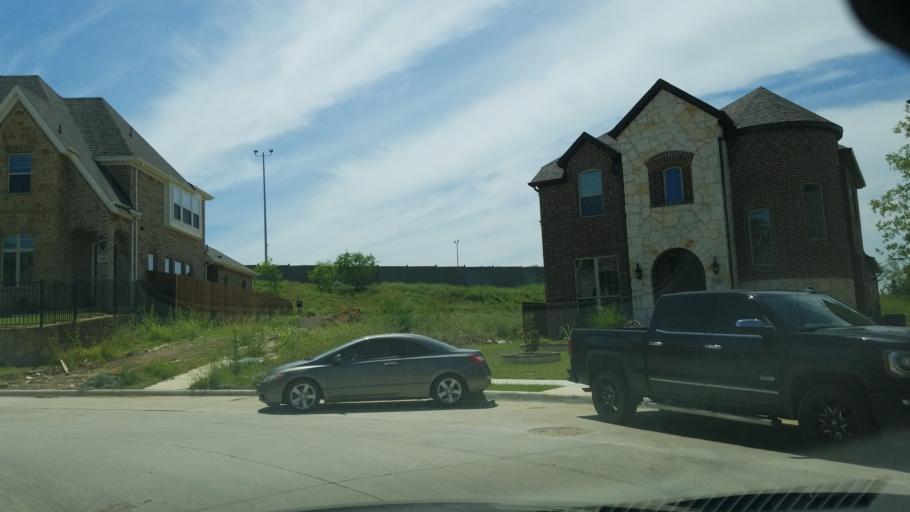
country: US
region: Texas
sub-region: Dallas County
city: Coppell
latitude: 32.8801
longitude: -96.9979
